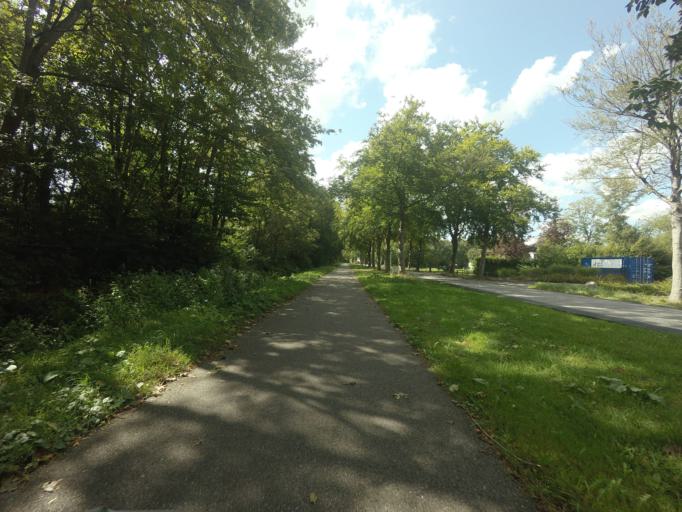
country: NL
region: Drenthe
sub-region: Gemeente Westerveld
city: Dwingeloo
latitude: 52.9549
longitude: 6.3249
